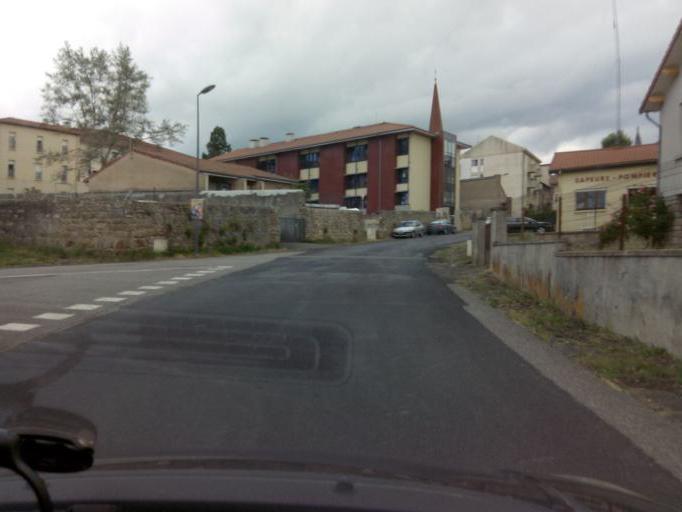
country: FR
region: Rhone-Alpes
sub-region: Departement de la Loire
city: Usson-en-Forez
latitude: 45.3876
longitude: 3.9416
